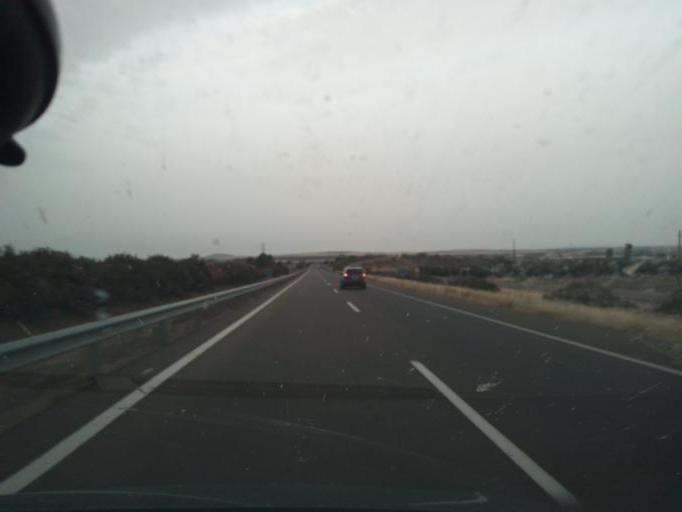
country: ES
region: Extremadura
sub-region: Provincia de Badajoz
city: San Pedro de Merida
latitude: 38.9496
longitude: -6.2140
